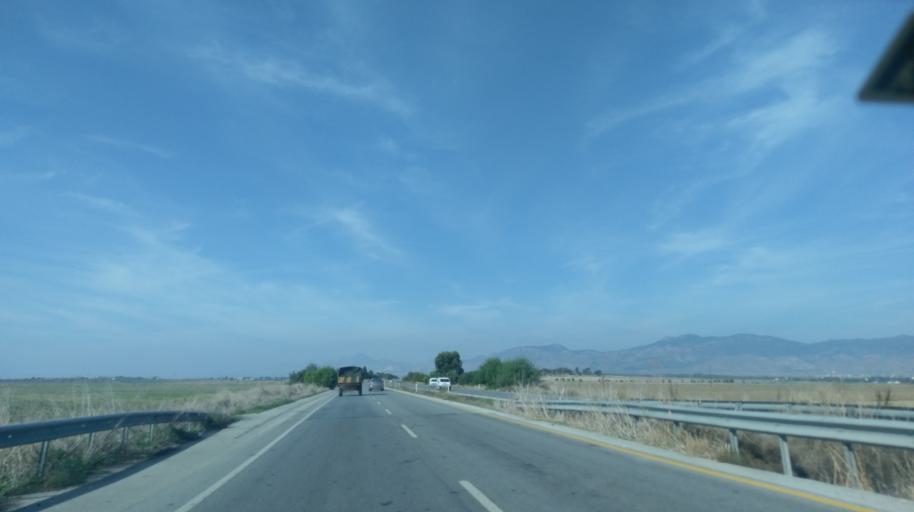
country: CY
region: Ammochostos
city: Lefkonoiko
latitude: 35.1908
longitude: 33.6262
